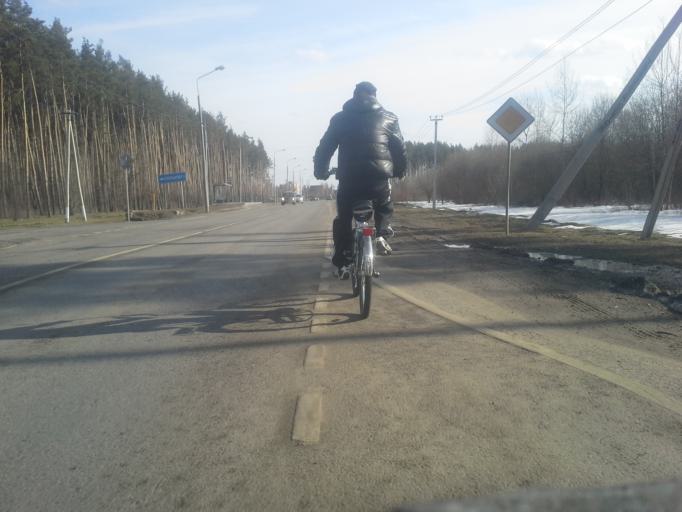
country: RU
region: Moskovskaya
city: Shcherbinka
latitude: 55.4829
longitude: 37.5206
